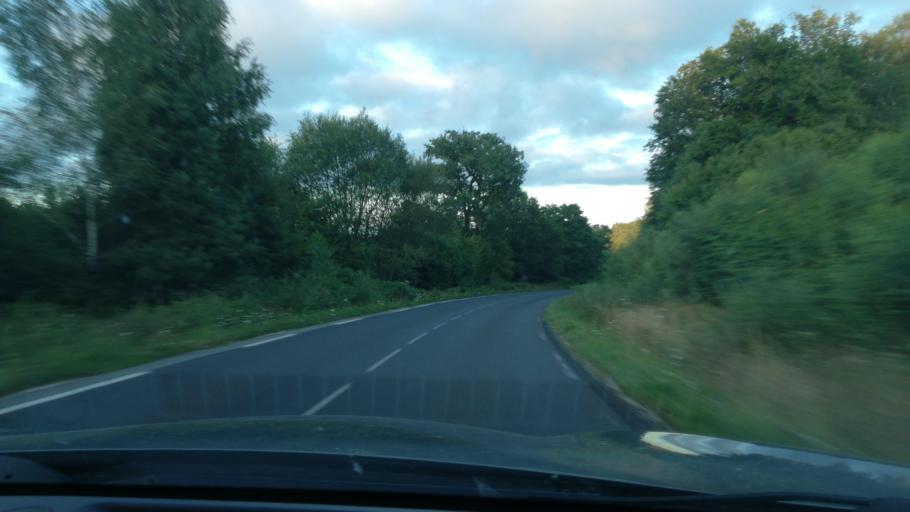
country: FR
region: Auvergne
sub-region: Departement du Cantal
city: Laroquebrou
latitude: 44.9603
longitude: 2.1650
